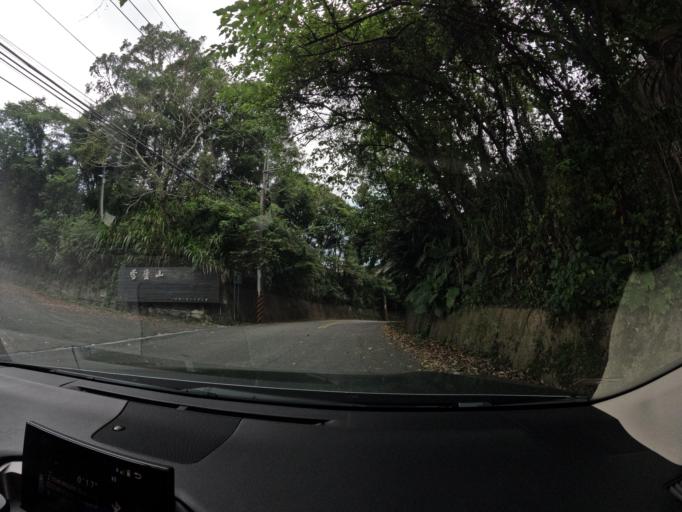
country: TW
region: Taiwan
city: Fengyuan
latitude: 24.3218
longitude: 120.8802
